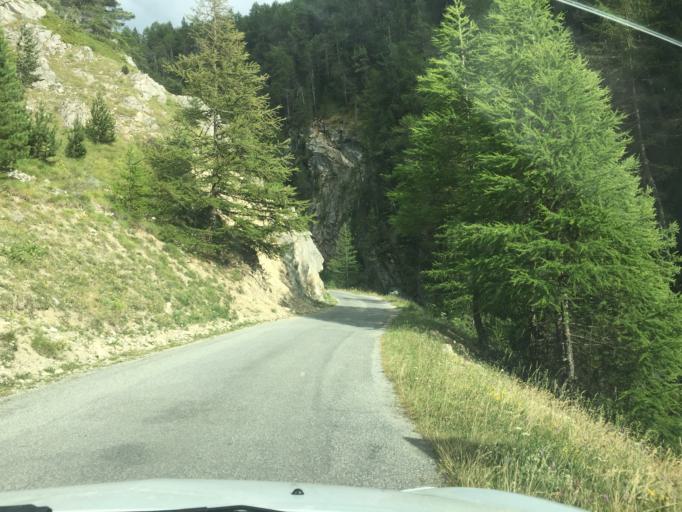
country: FR
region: Provence-Alpes-Cote d'Azur
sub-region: Departement des Hautes-Alpes
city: Guillestre
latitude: 44.6736
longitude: 6.7898
